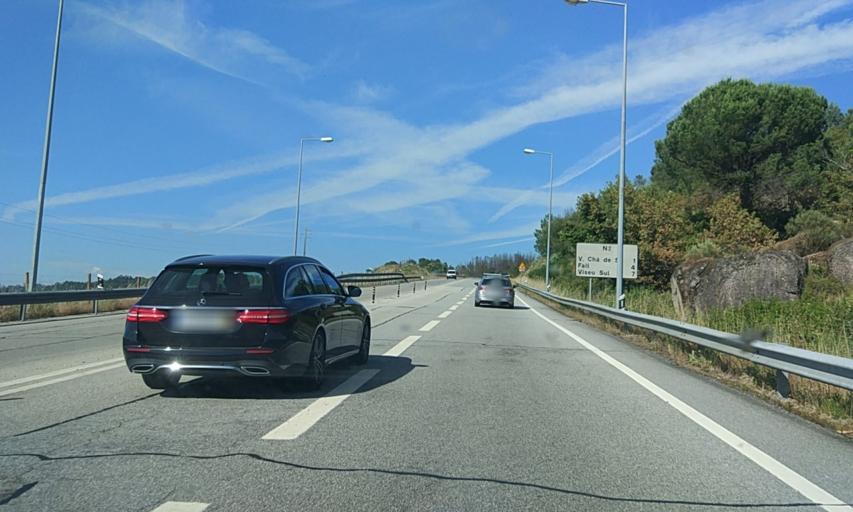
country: PT
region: Viseu
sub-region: Viseu
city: Viseu
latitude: 40.6039
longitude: -7.9743
